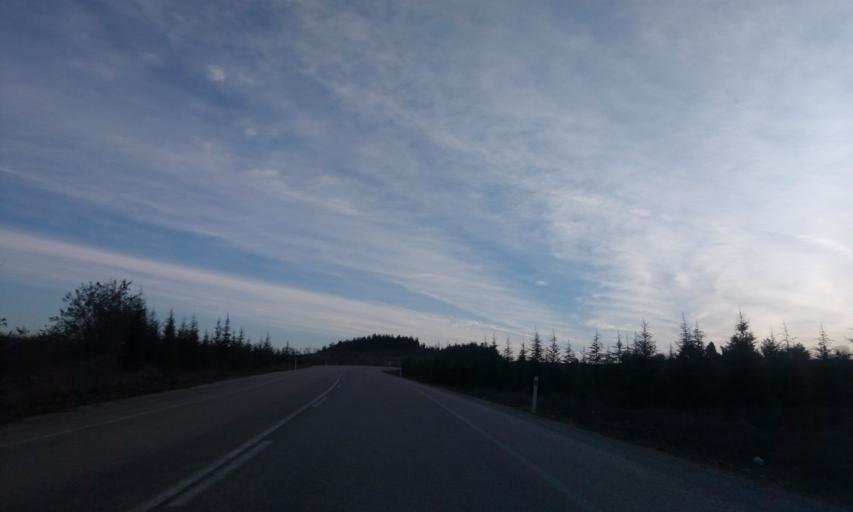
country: TR
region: Bilecik
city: Kuplu
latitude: 40.1108
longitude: 30.0708
